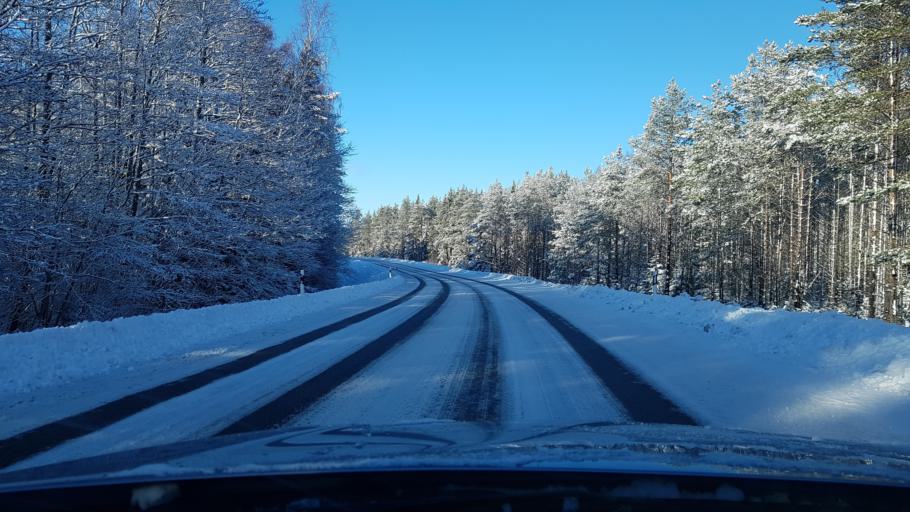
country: EE
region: Hiiumaa
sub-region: Kaerdla linn
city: Kardla
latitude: 58.9719
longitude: 22.7678
